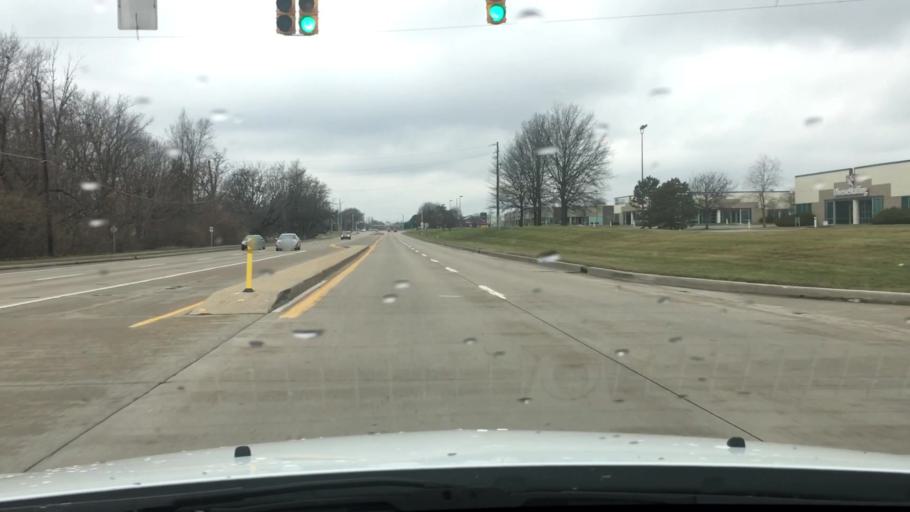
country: US
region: Indiana
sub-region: Boone County
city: Zionsville
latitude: 39.8819
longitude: -86.2530
